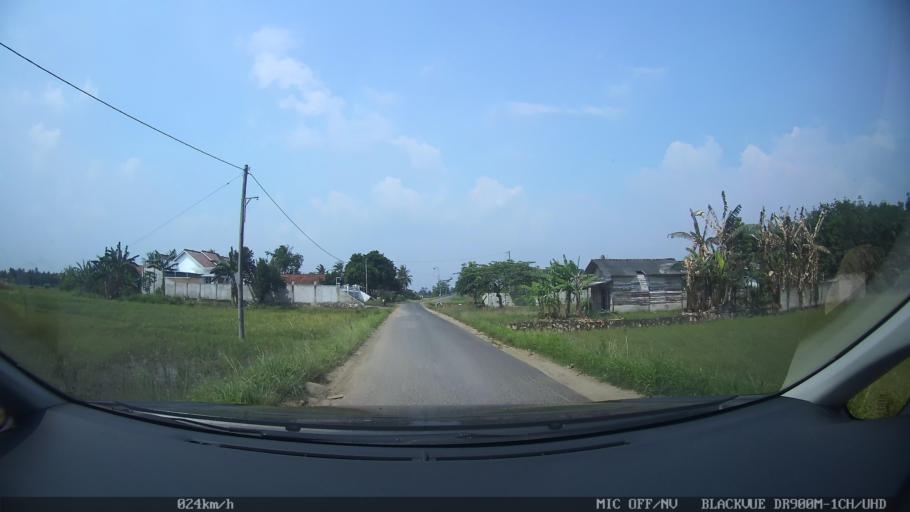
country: ID
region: Lampung
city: Natar
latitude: -5.3033
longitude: 105.2386
